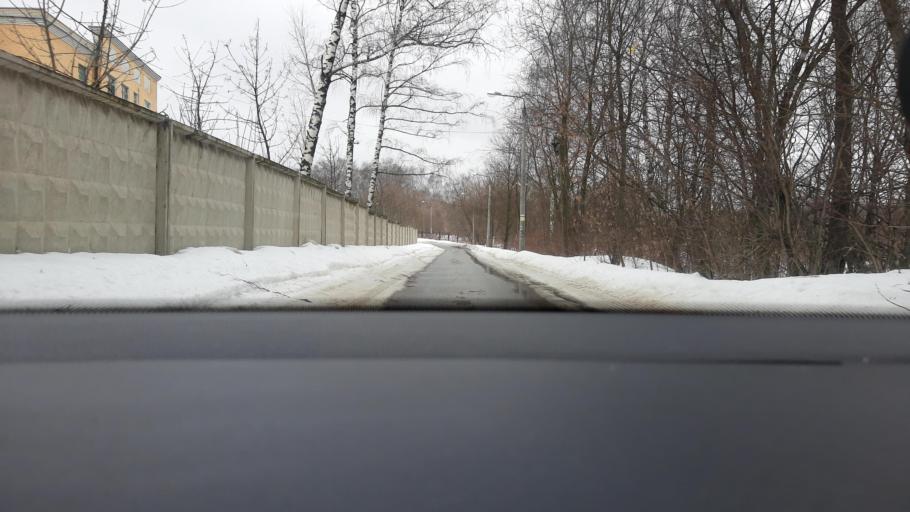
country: RU
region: Moskovskaya
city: Druzhba
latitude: 55.8888
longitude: 37.7595
